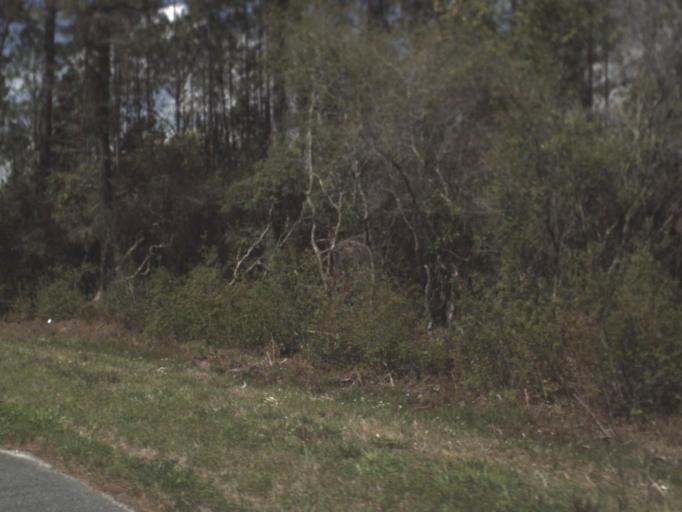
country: US
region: Florida
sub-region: Gadsden County
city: Midway
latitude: 30.3889
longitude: -84.6205
